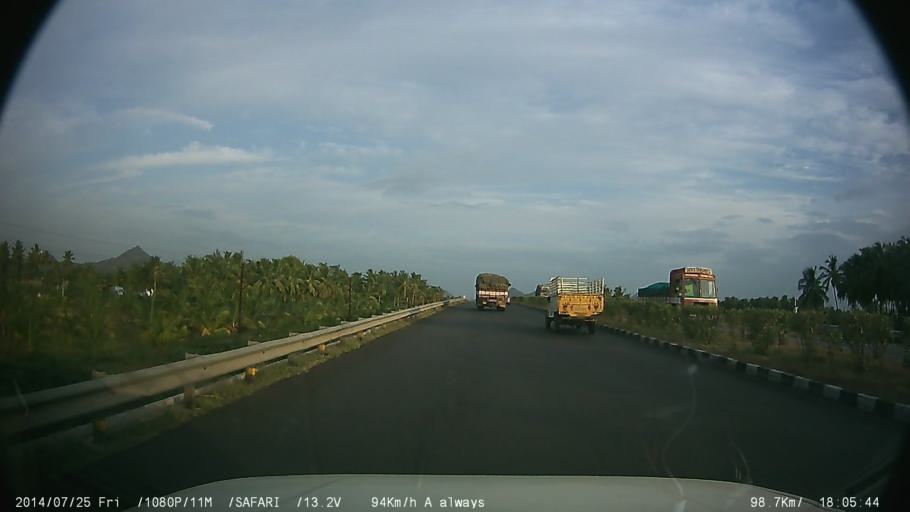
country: IN
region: Tamil Nadu
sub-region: Krishnagiri
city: Kaverippattanam
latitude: 12.4347
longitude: 78.2231
